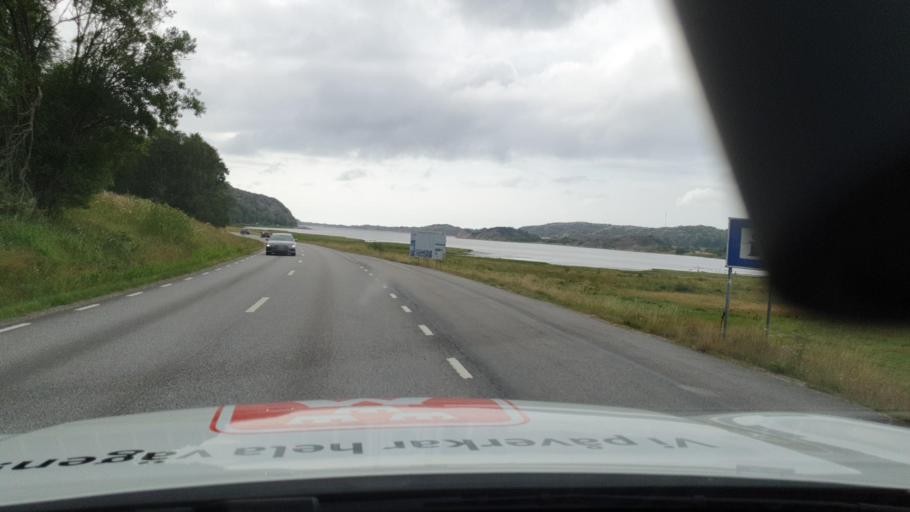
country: SE
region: Vaestra Goetaland
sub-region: Sotenas Kommun
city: Hunnebostrand
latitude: 58.4876
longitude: 11.3644
